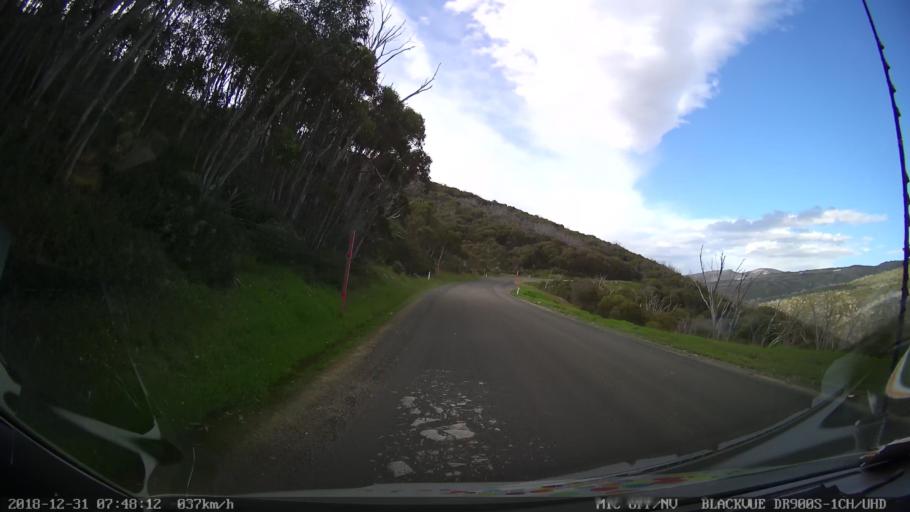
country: AU
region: New South Wales
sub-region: Snowy River
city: Jindabyne
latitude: -36.3673
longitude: 148.3926
